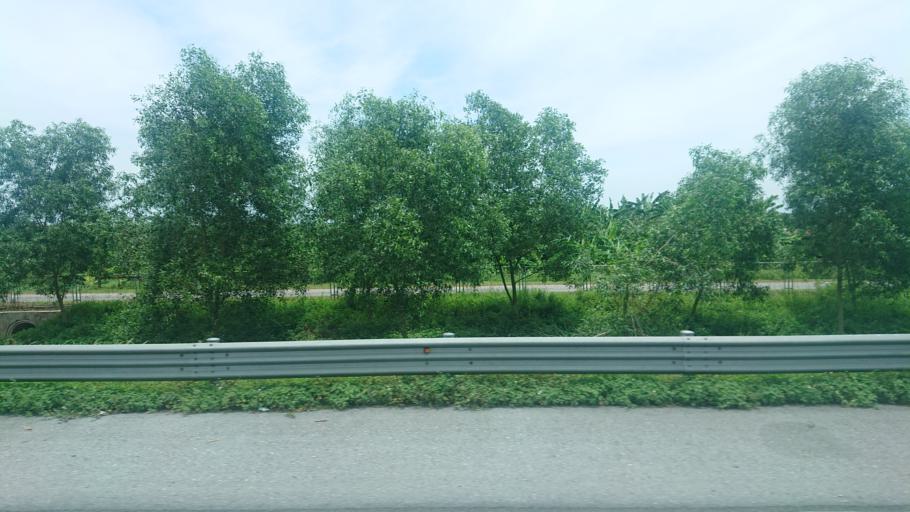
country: VN
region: Hai Phong
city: An Lao
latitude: 20.8174
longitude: 106.4868
